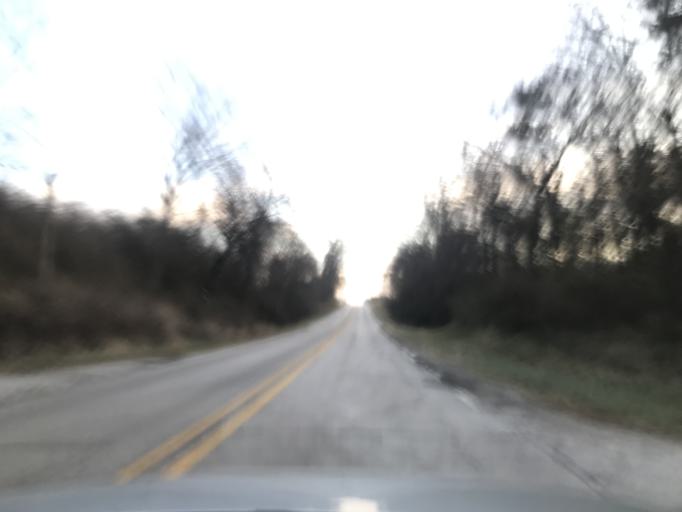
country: US
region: Illinois
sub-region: Henderson County
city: Oquawka
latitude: 40.9604
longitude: -90.8640
